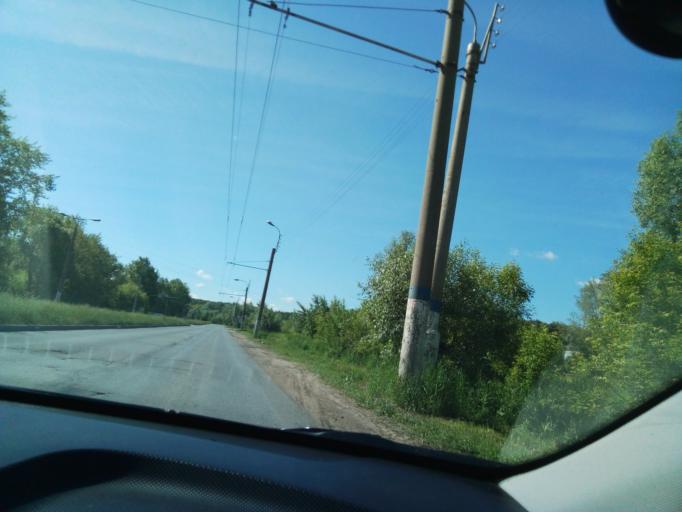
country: RU
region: Chuvashia
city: Novocheboksarsk
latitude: 56.0888
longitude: 47.5017
